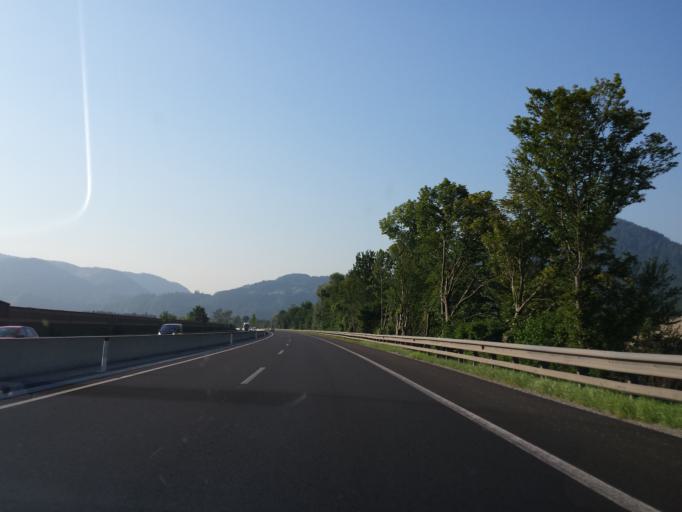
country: AT
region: Styria
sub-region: Politischer Bezirk Graz-Umgebung
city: Frohnleiten
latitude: 47.2458
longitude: 15.3172
